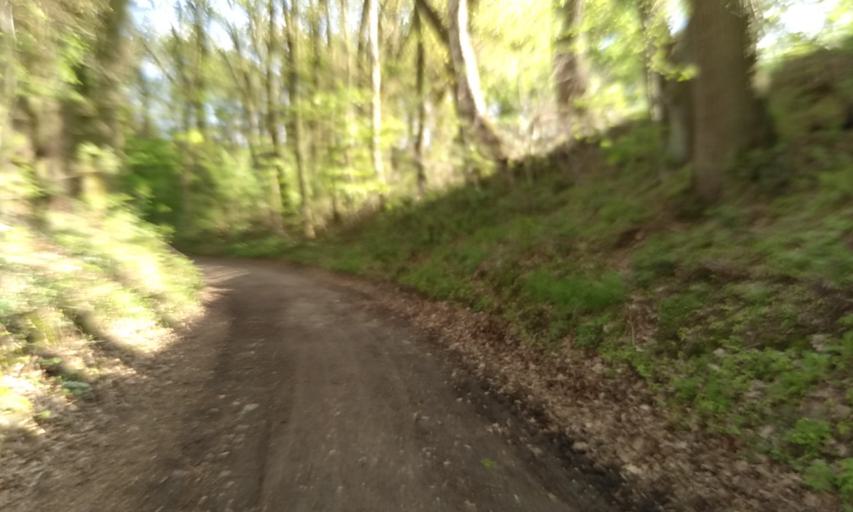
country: DE
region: Lower Saxony
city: Regesbostel
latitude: 53.4107
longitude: 9.6512
